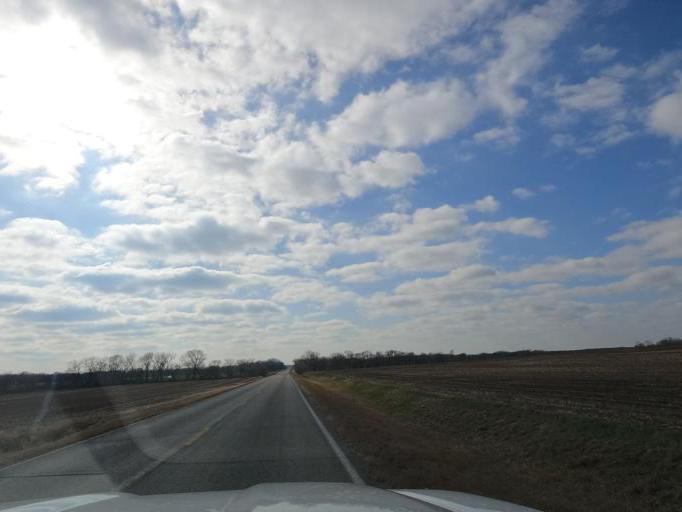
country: US
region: Kansas
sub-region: McPherson County
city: Inman
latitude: 38.2320
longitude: -97.8708
